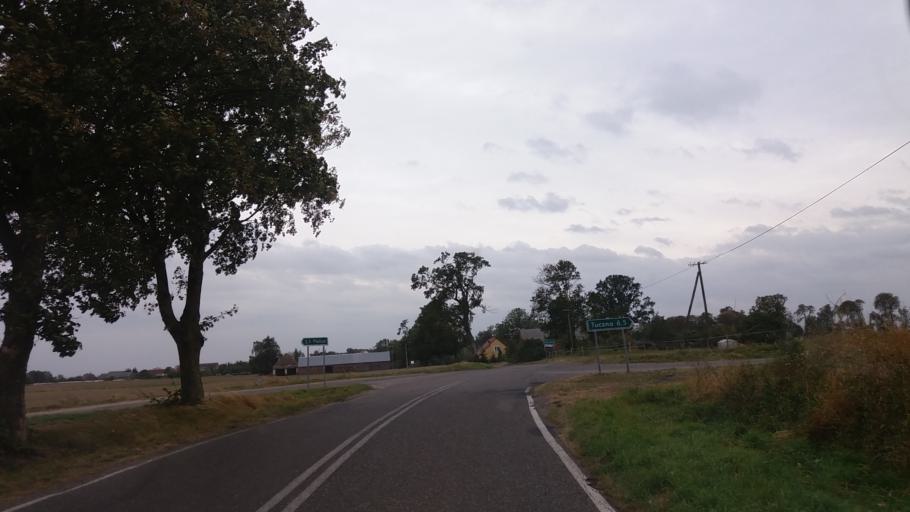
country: PL
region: Lubusz
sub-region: Powiat strzelecko-drezdenecki
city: Strzelce Krajenskie
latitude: 52.9335
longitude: 15.5613
